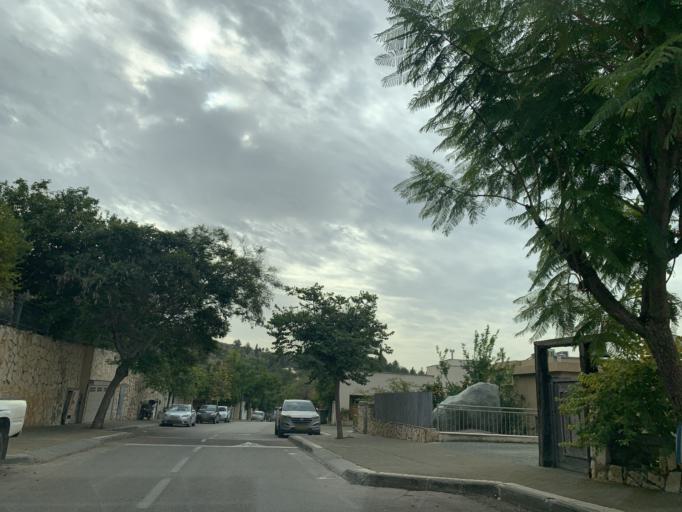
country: IL
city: Nirit
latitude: 32.1481
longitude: 34.9811
